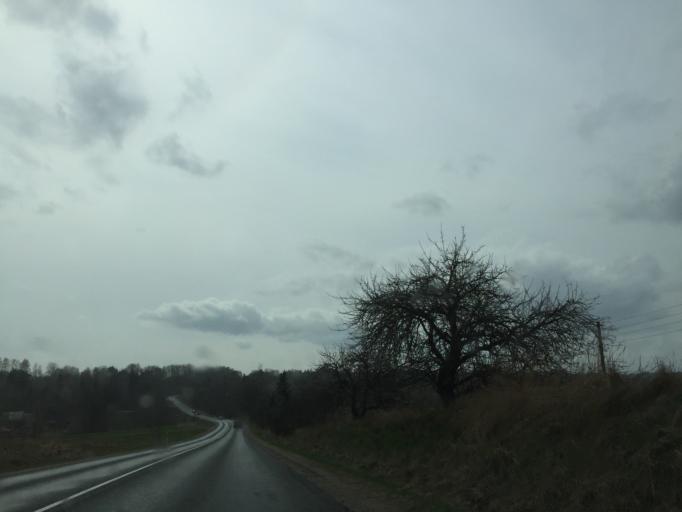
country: LV
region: Priekuli
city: Priekuli
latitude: 57.3381
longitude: 25.3326
